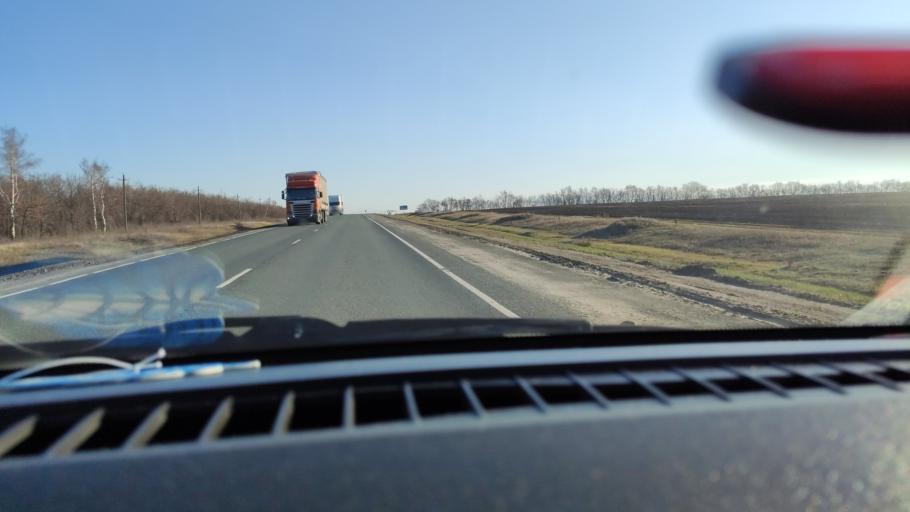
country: RU
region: Saratov
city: Alekseyevka
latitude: 52.2631
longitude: 47.9226
